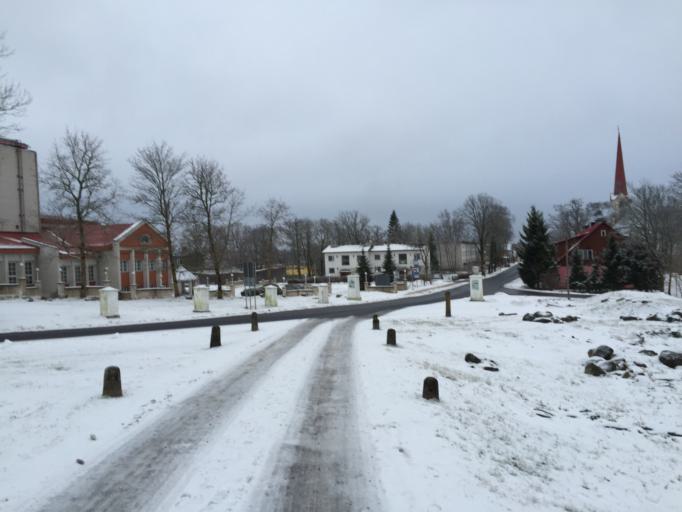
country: EE
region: Laeaene
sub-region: Lihula vald
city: Lihula
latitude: 58.6926
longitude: 23.8382
